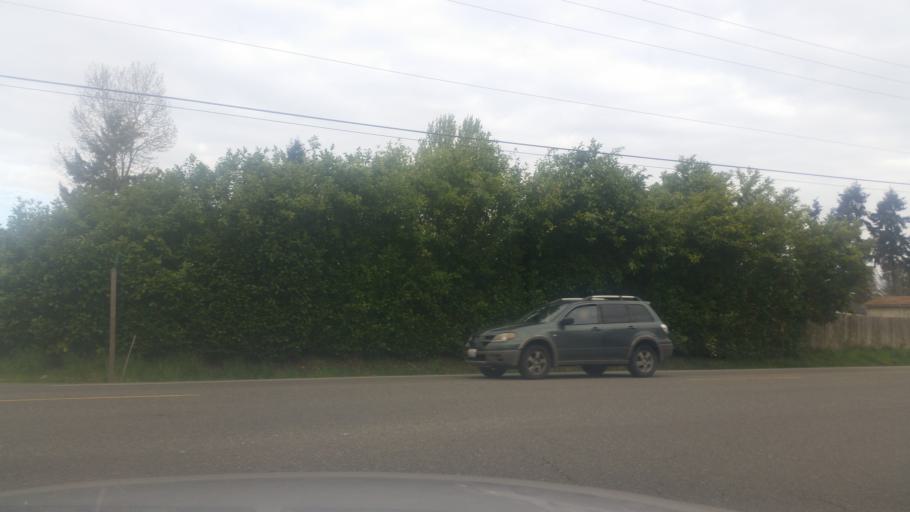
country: US
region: Washington
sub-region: Pierce County
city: South Hill
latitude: 47.1141
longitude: -122.2666
